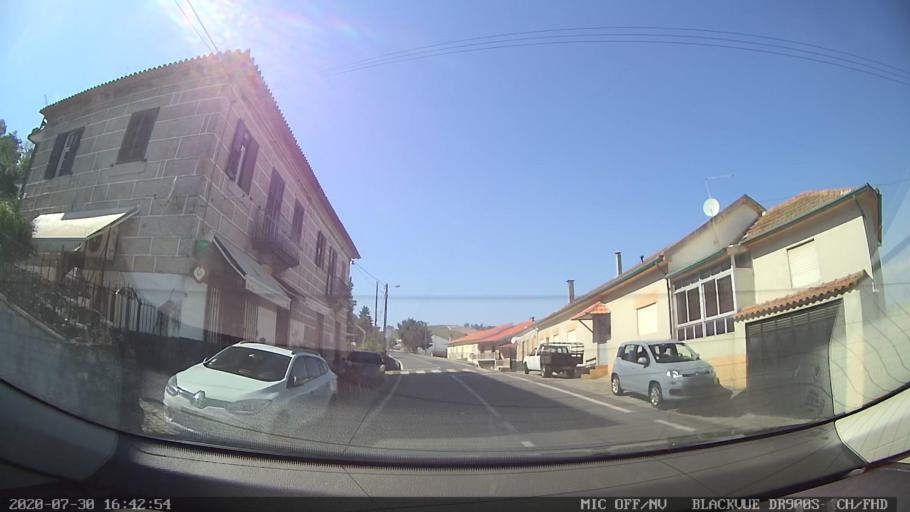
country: PT
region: Vila Real
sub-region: Sabrosa
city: Sabrosa
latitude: 41.2912
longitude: -7.4790
